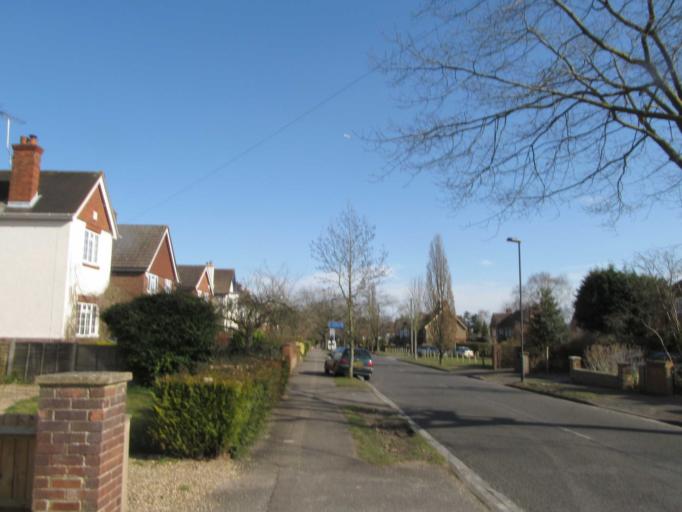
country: GB
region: England
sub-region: Royal Borough of Windsor and Maidenhead
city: Maidenhead
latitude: 51.5311
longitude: -0.7442
